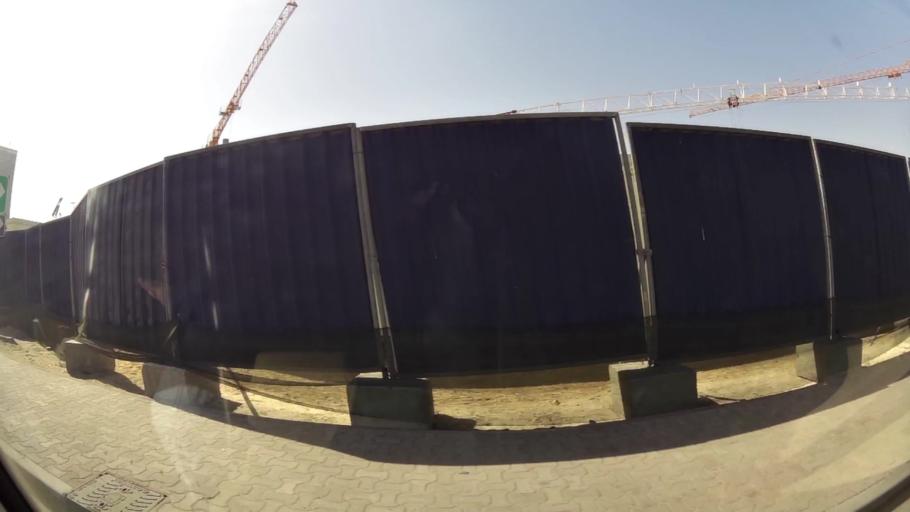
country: AE
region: Ash Shariqah
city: Sharjah
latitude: 25.2779
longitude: 55.3007
